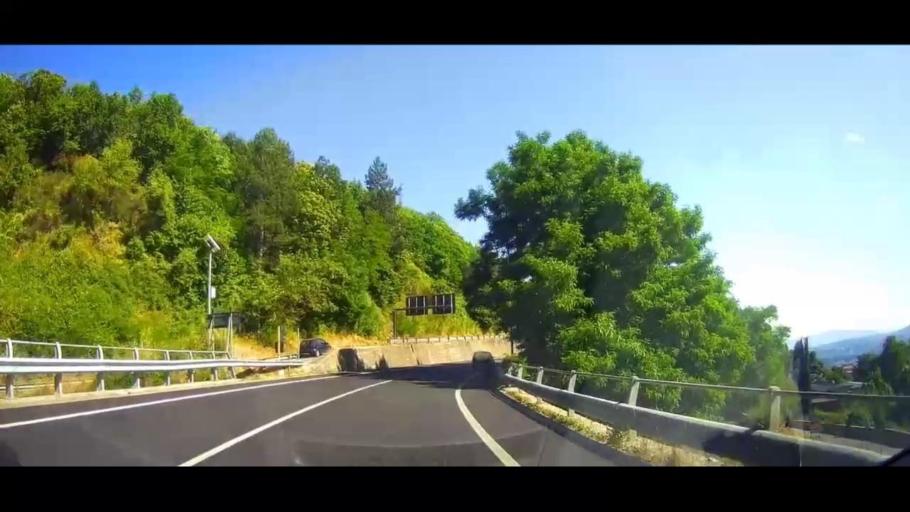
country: IT
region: Calabria
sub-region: Provincia di Cosenza
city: Spezzano della Sila
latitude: 39.2994
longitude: 16.3422
